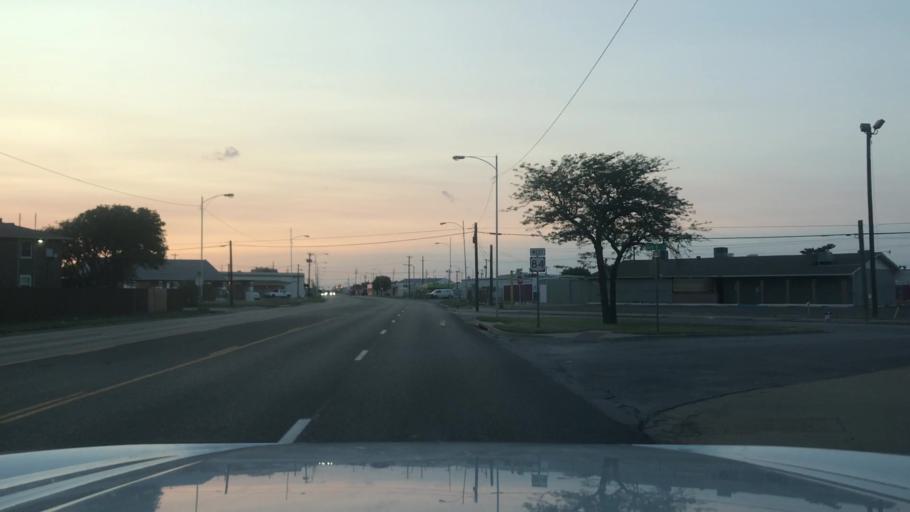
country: US
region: Texas
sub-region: Lubbock County
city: Lubbock
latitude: 33.5956
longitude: -101.8564
